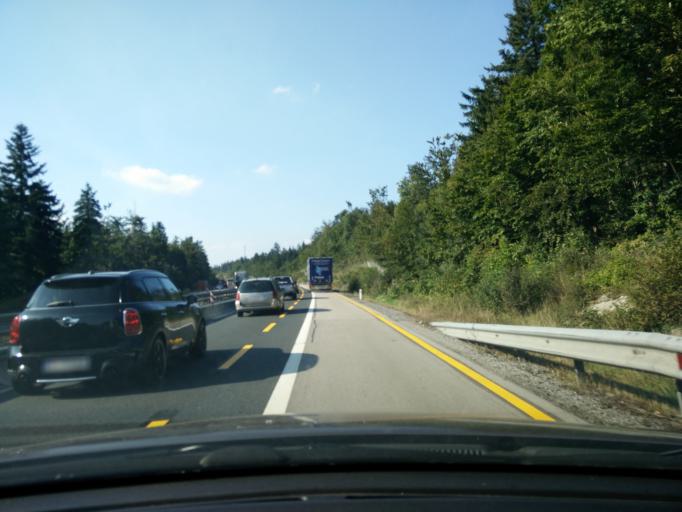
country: SI
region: Logatec
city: Logatec
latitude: 45.8679
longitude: 14.2703
